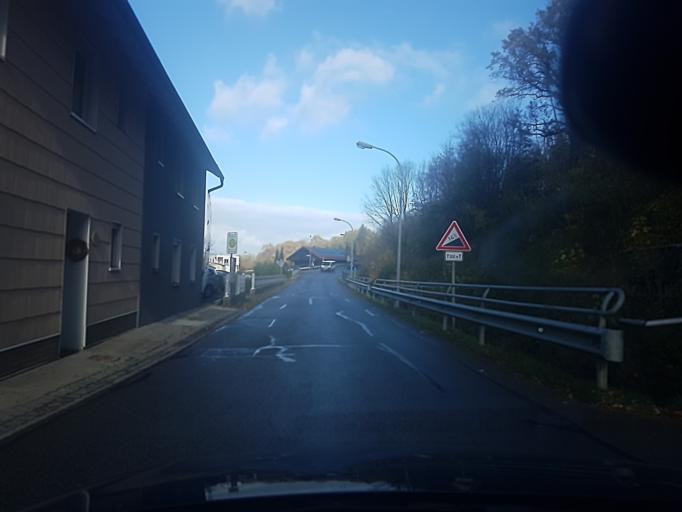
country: DE
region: Bavaria
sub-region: Lower Bavaria
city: Loiching
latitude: 48.6224
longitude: 12.4617
